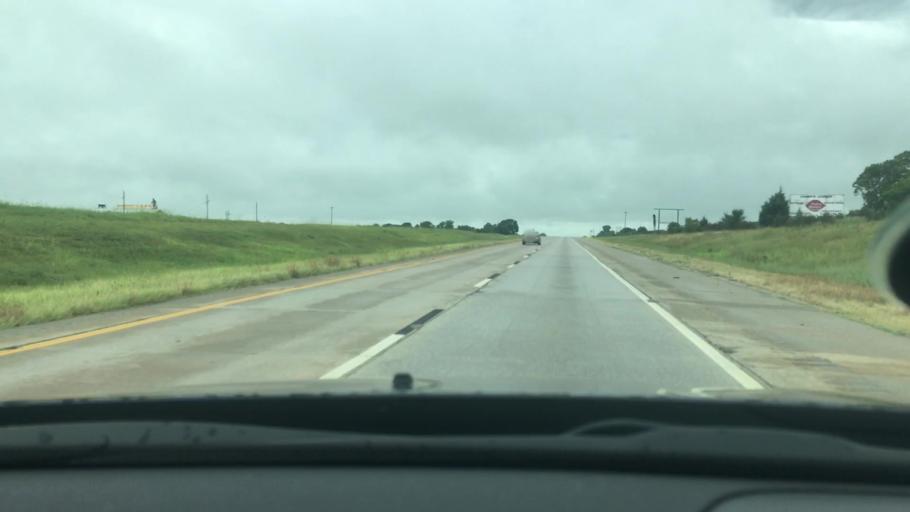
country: US
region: Oklahoma
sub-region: Atoka County
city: Atoka
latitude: 34.2185
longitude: -96.2300
